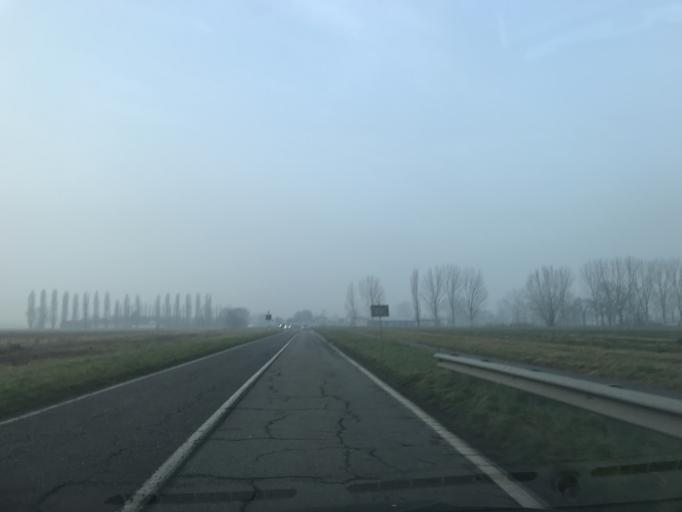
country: IT
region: Lombardy
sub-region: Provincia di Lodi
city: Ossago Lodigiano
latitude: 45.2579
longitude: 9.5363
